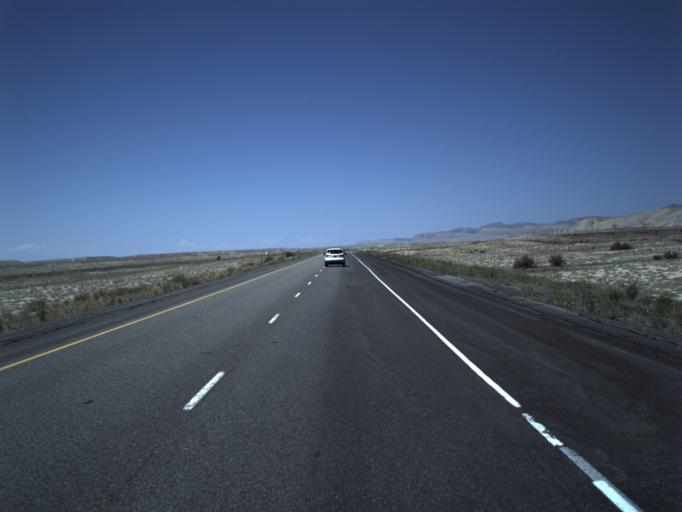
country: US
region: Utah
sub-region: Grand County
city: Moab
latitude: 38.9345
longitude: -109.4487
